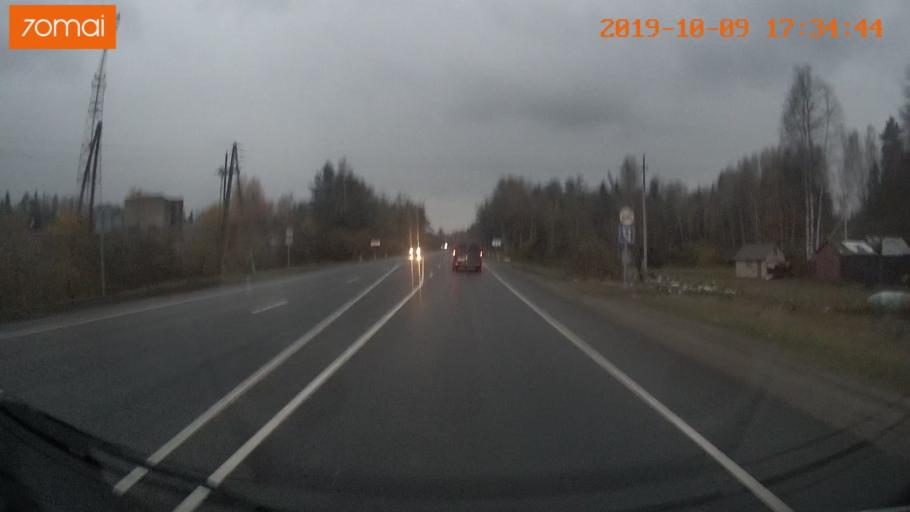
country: RU
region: Ivanovo
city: Bogorodskoye
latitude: 57.1038
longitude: 41.0091
